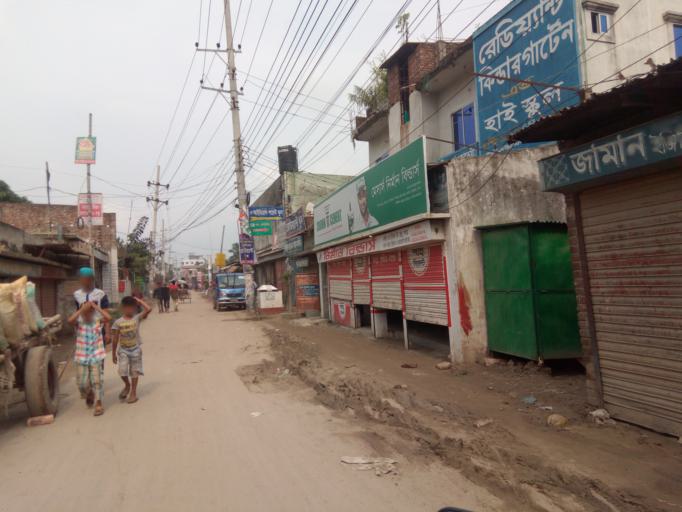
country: BD
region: Dhaka
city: Paltan
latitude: 23.7447
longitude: 90.4490
